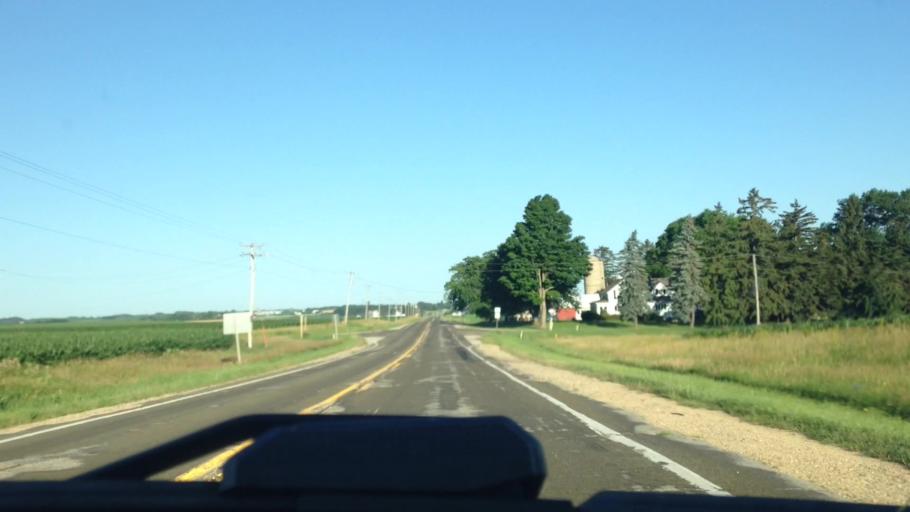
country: US
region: Wisconsin
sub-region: Columbia County
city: Poynette
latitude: 43.3378
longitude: -89.4210
